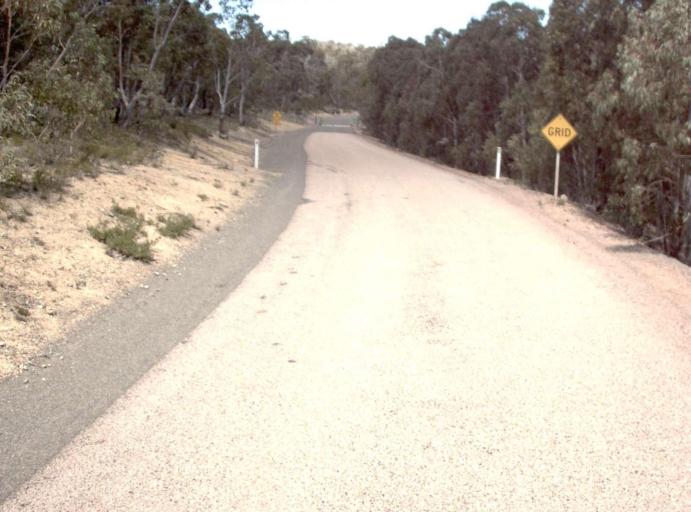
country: AU
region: New South Wales
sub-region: Snowy River
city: Jindabyne
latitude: -37.0729
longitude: 148.2809
